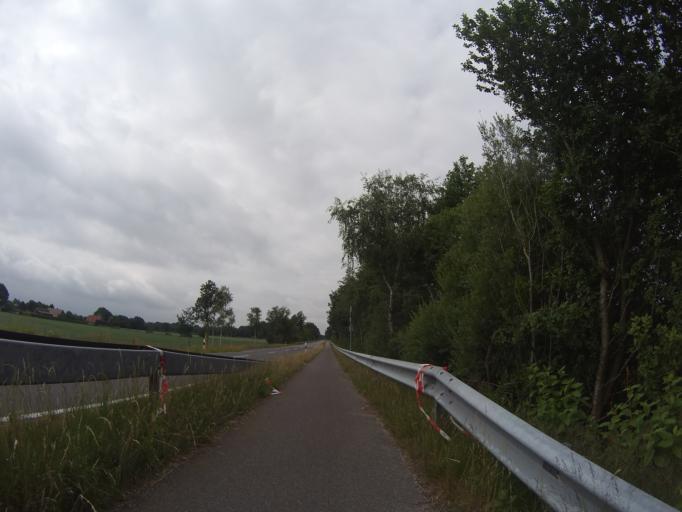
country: DE
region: Lower Saxony
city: Haren
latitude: 52.7089
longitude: 7.1626
